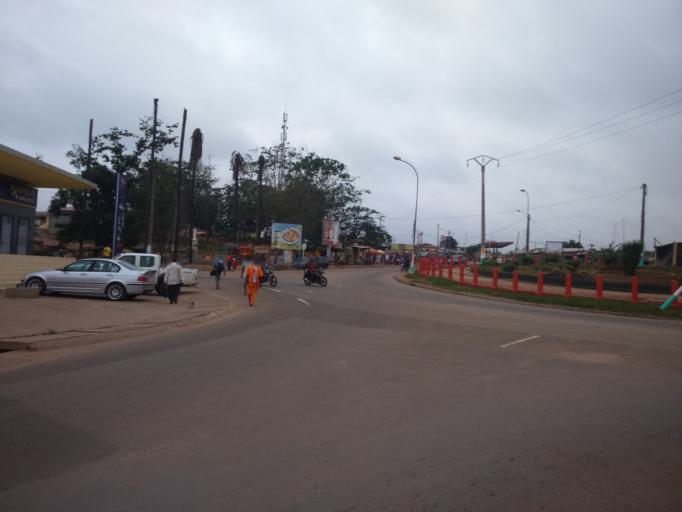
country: CI
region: Agneby
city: Agboville
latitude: 5.9314
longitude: -4.2139
